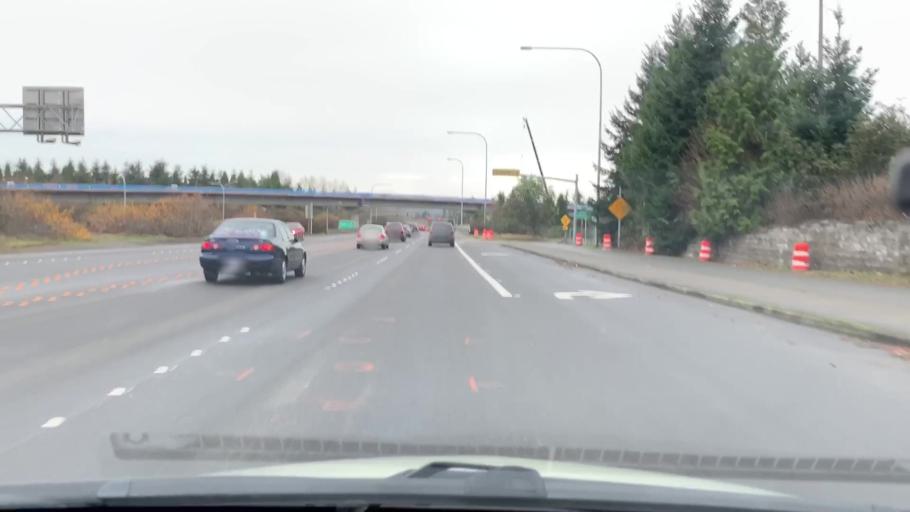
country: US
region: Washington
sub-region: King County
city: Redmond
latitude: 47.6359
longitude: -122.1431
